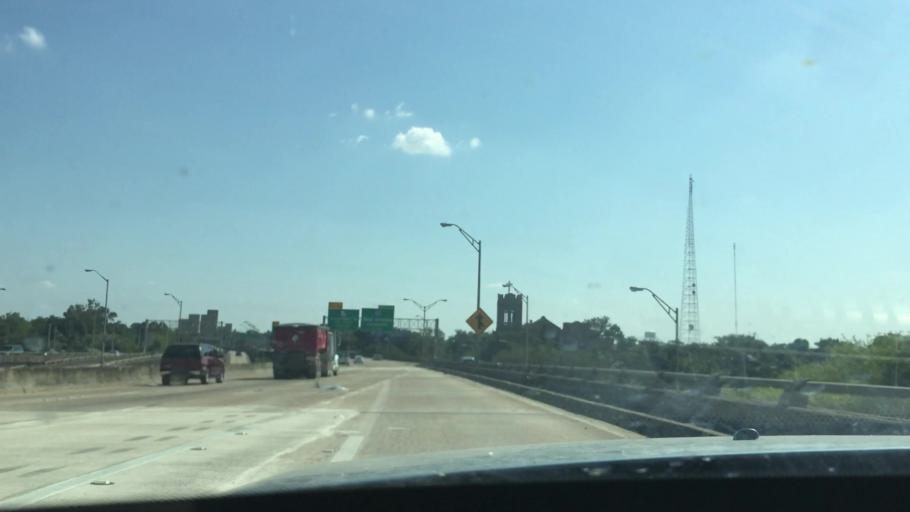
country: US
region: Louisiana
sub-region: East Baton Rouge Parish
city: Baton Rouge
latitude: 30.4492
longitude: -91.1806
